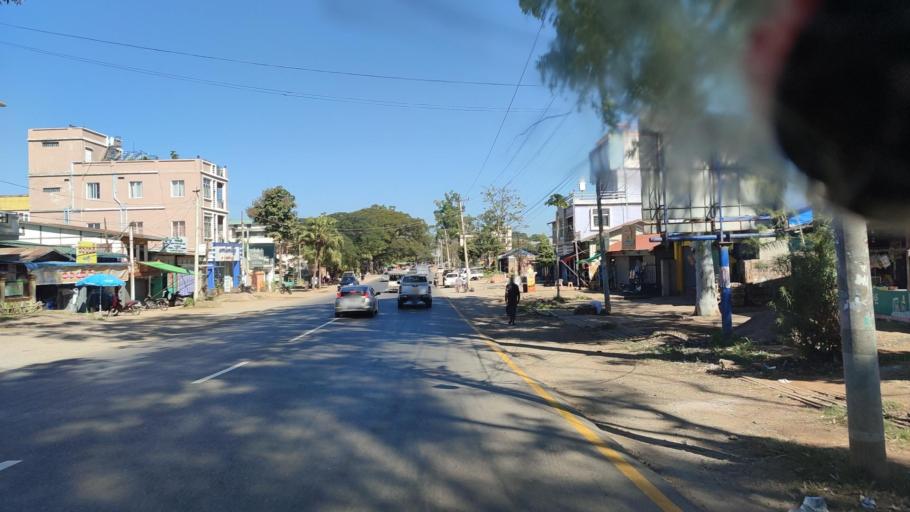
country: MM
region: Mandalay
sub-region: Pyin Oo Lwin District
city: Pyin Oo Lwin
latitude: 21.9737
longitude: 96.4065
